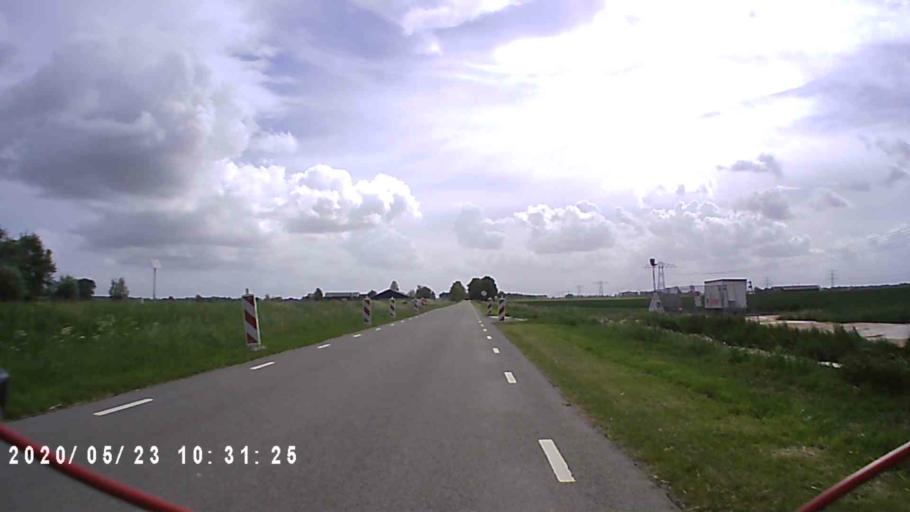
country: NL
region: Groningen
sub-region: Gemeente Appingedam
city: Appingedam
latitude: 53.3022
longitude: 6.8675
